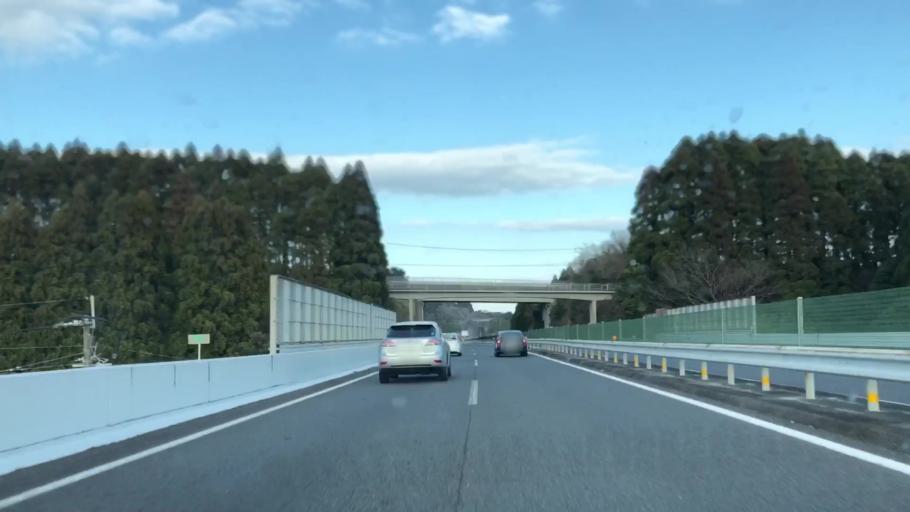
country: JP
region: Miyazaki
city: Miyazaki-shi
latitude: 31.8573
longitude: 131.3758
